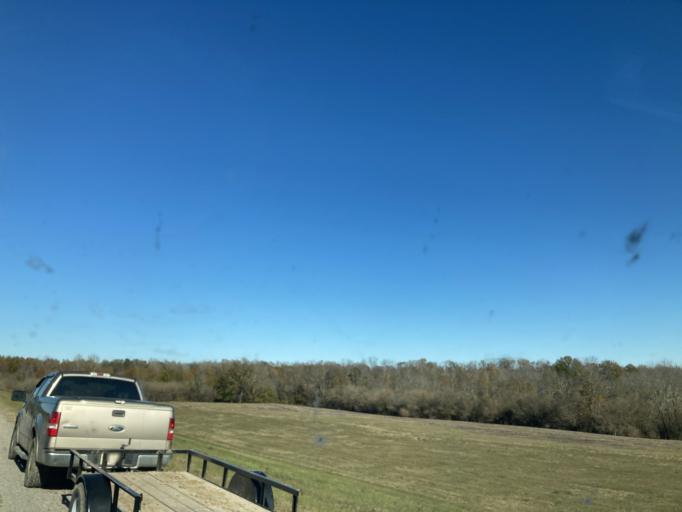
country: US
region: Mississippi
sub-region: Sharkey County
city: Rolling Fork
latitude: 32.7011
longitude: -90.6817
